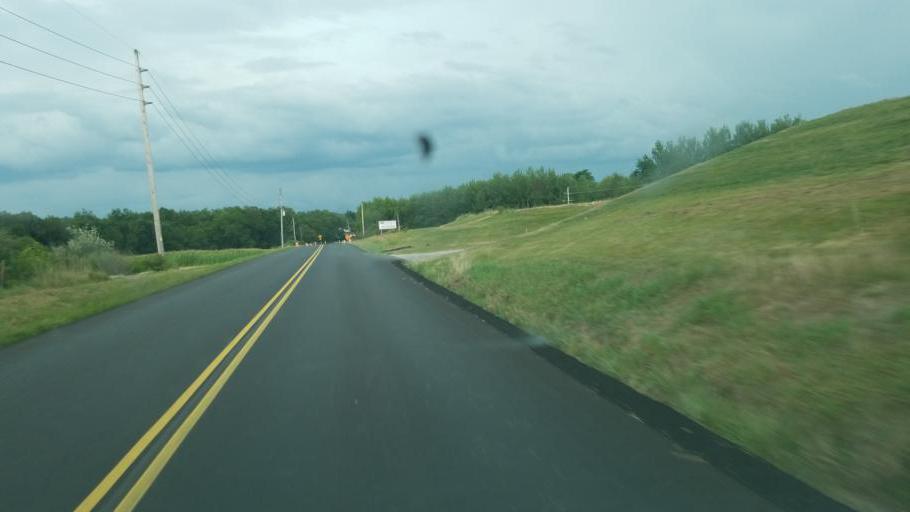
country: US
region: Pennsylvania
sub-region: Clarion County
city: Knox
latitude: 41.2411
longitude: -79.5333
